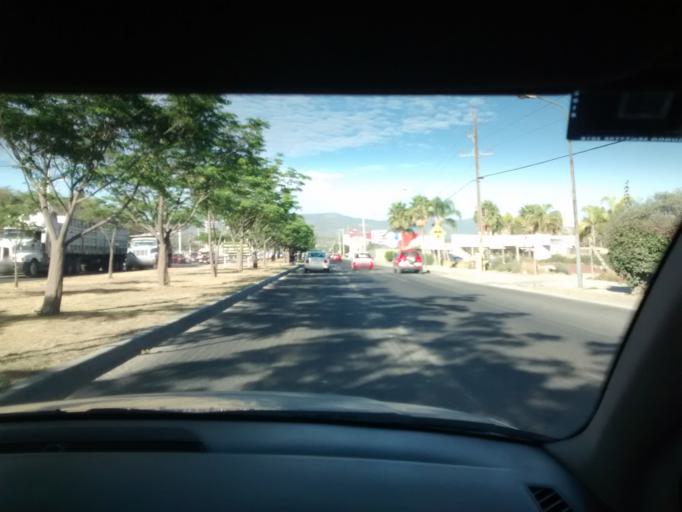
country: MX
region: Puebla
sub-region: Santiago Miahuatlan
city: San Jose Monte Chiquito
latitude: 18.4796
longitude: -97.4205
